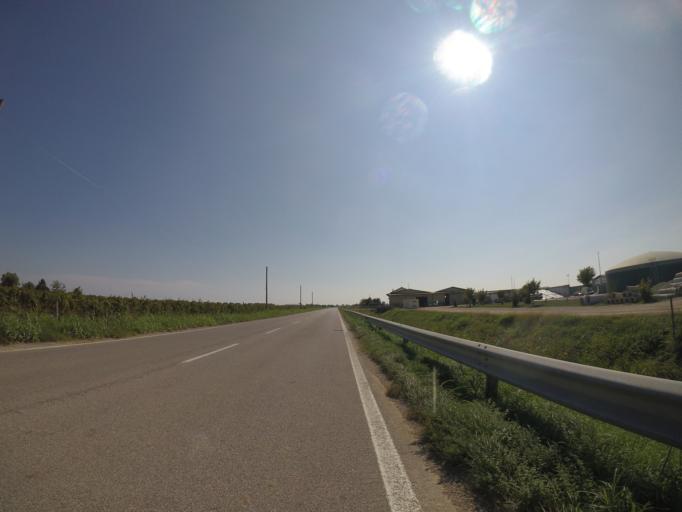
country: IT
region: Friuli Venezia Giulia
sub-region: Provincia di Udine
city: Carlino
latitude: 45.7971
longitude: 13.1660
